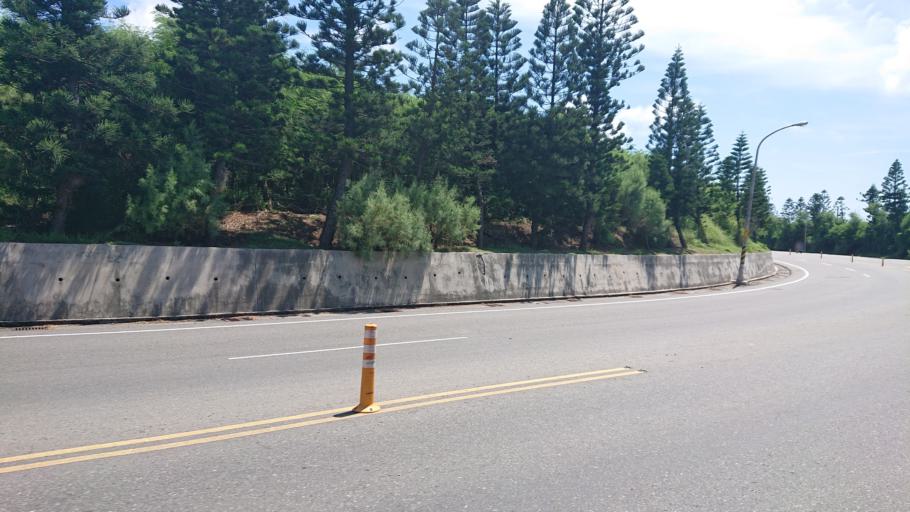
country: TW
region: Taiwan
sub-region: Penghu
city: Ma-kung
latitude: 23.6612
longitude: 119.5588
